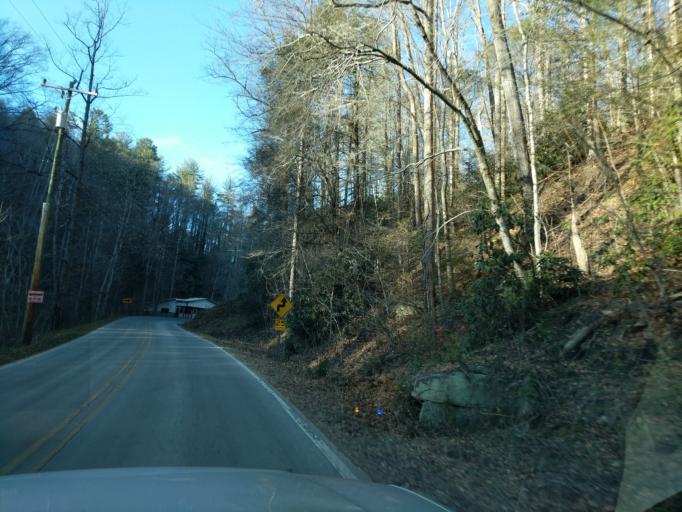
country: US
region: North Carolina
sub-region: Henderson County
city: Edneyville
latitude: 35.4536
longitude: -82.2973
